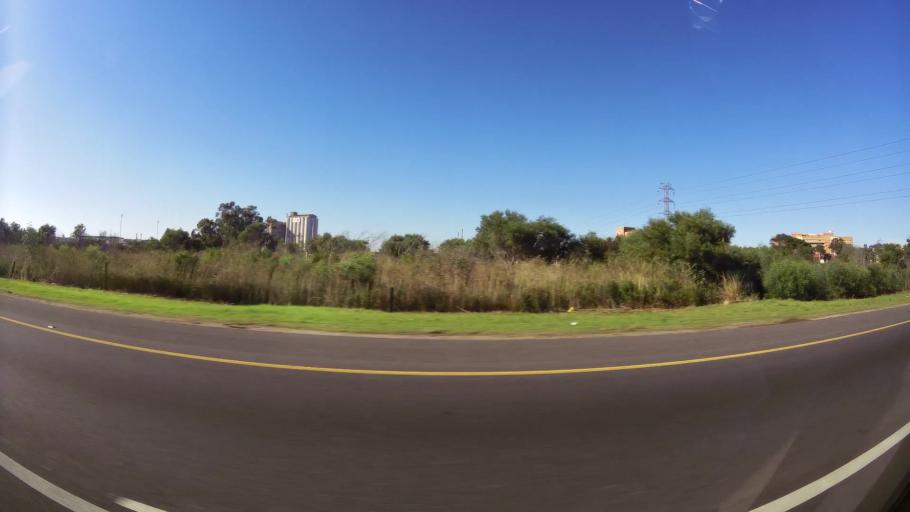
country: ZA
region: Eastern Cape
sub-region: Nelson Mandela Bay Metropolitan Municipality
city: Port Elizabeth
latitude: -33.9211
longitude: 25.5700
